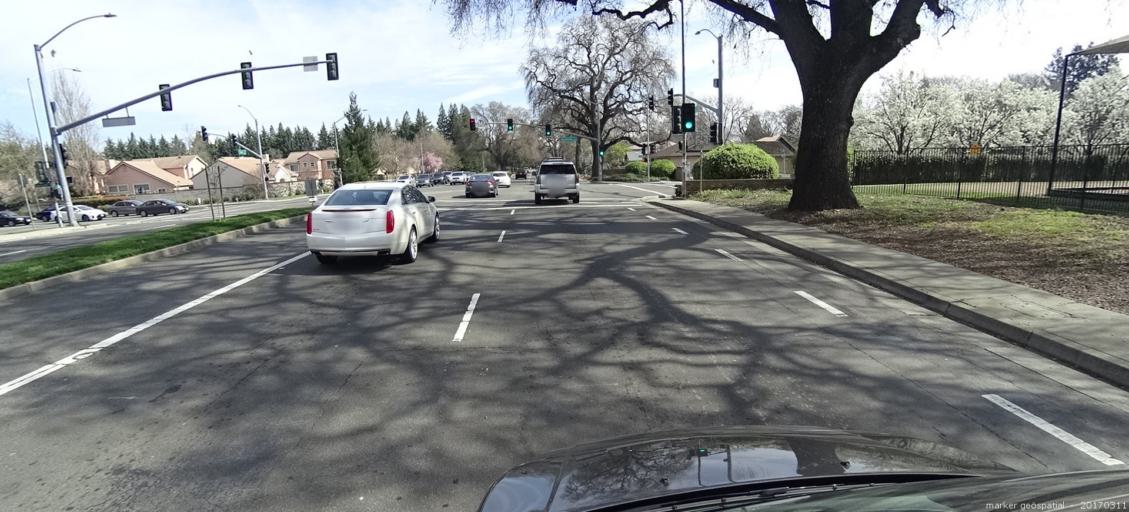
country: US
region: California
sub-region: Sacramento County
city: Parkway
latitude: 38.4802
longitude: -121.5168
